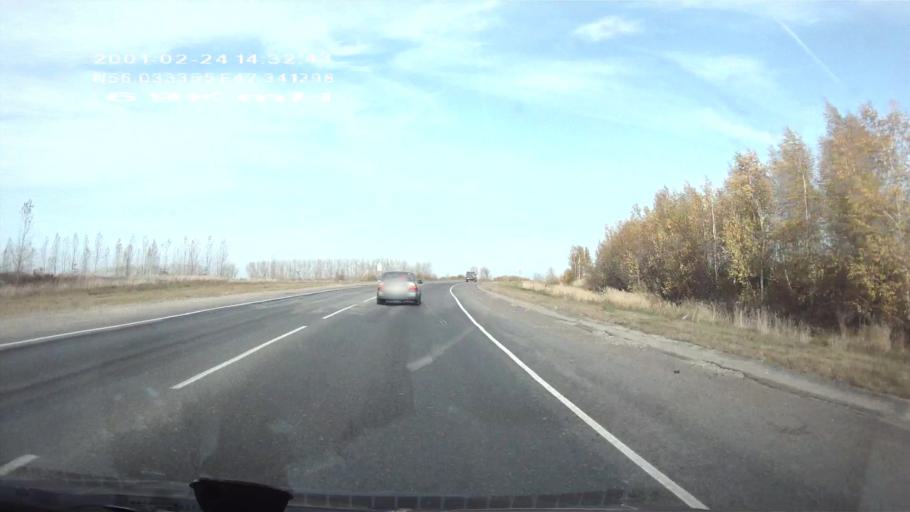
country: RU
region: Chuvashia
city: Kugesi
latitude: 56.0331
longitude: 47.3410
